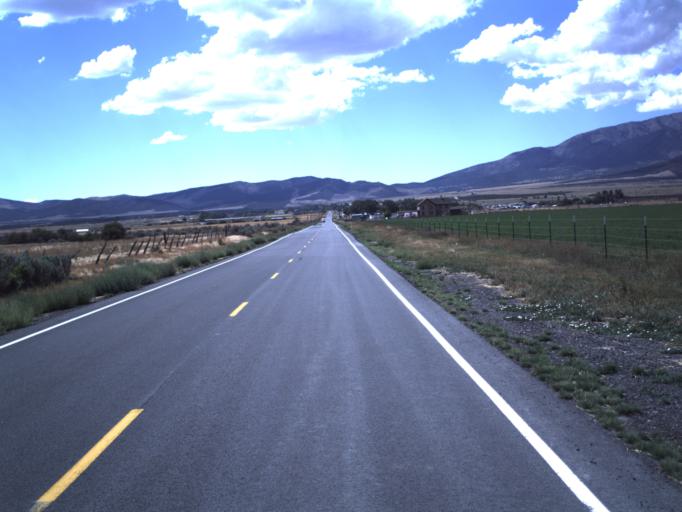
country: US
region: Utah
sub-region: Tooele County
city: Tooele
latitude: 40.3368
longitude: -112.4308
